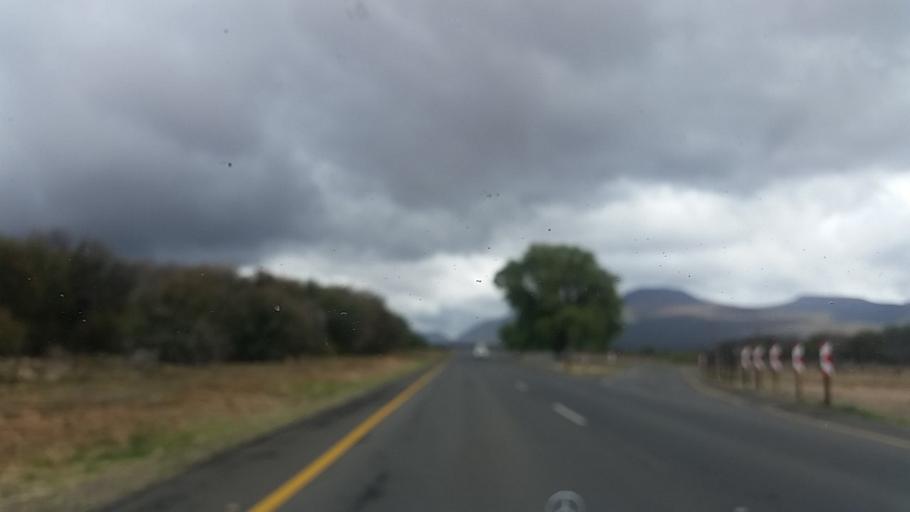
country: ZA
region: Eastern Cape
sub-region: Cacadu District Municipality
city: Graaff-Reinet
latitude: -32.2086
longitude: 24.5485
